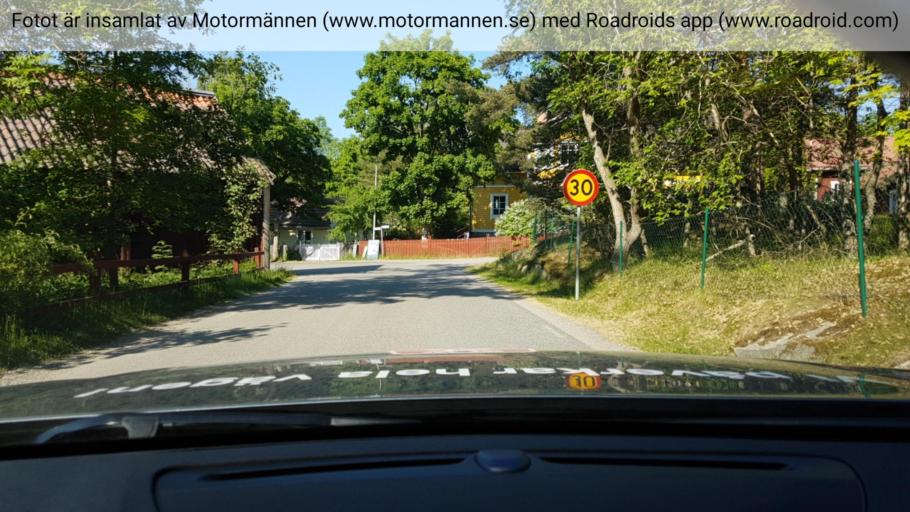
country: SE
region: Stockholm
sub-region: Varmdo Kommun
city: Holo
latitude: 59.2903
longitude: 18.6884
